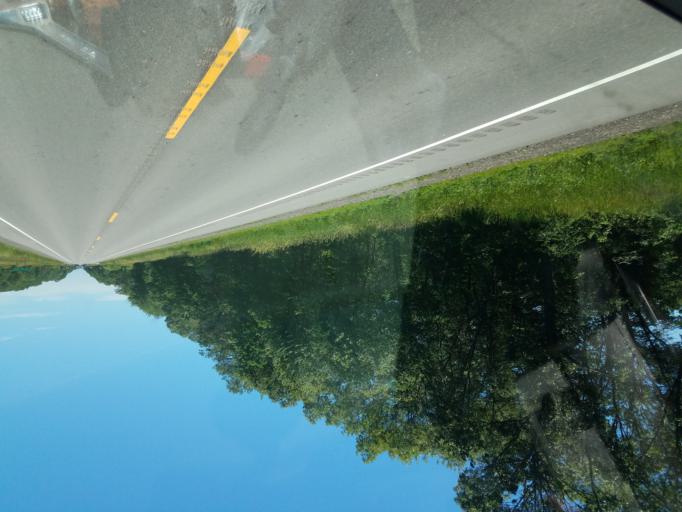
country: US
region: Wisconsin
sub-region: Juneau County
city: New Lisbon
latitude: 44.0256
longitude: -90.2328
